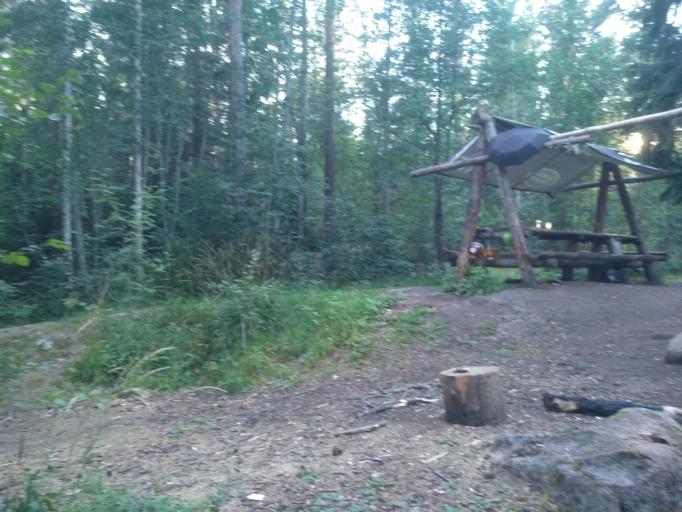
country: RU
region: Leningrad
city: Kuznechnoye
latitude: 61.1709
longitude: 29.7130
